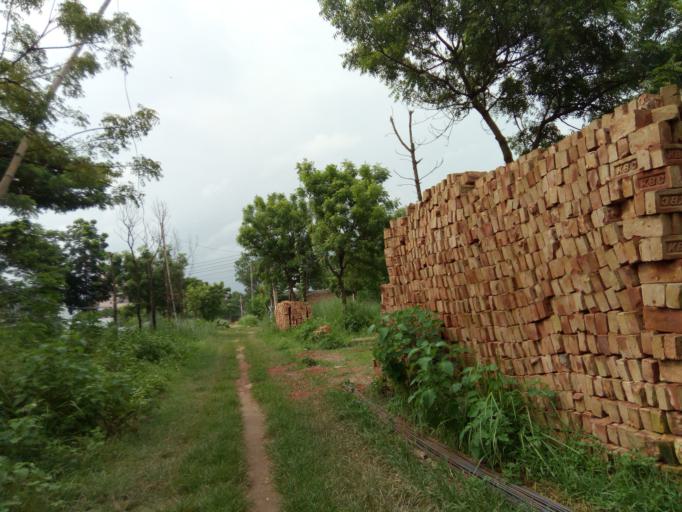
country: BD
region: Dhaka
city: Azimpur
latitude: 23.7543
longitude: 90.3420
